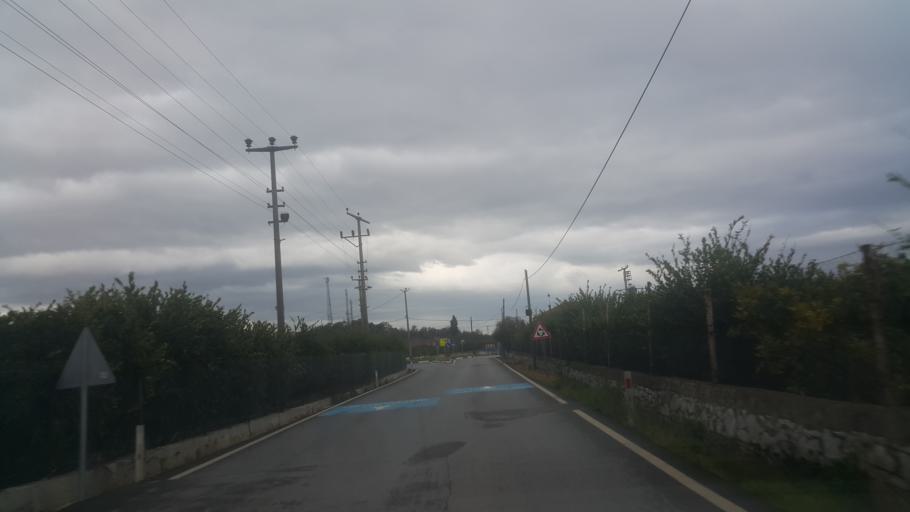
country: TR
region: Izmir
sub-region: Seferihisar
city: Seferhisar
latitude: 38.1892
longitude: 26.8075
